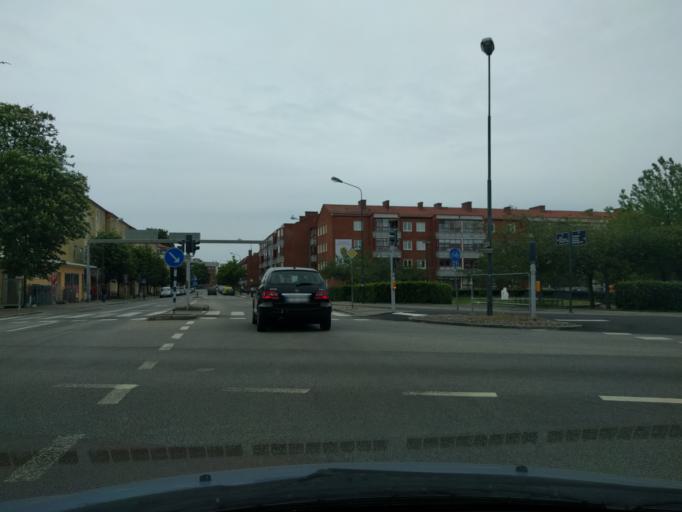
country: SE
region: Skane
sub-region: Malmo
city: Malmoe
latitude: 55.5904
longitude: 13.0281
